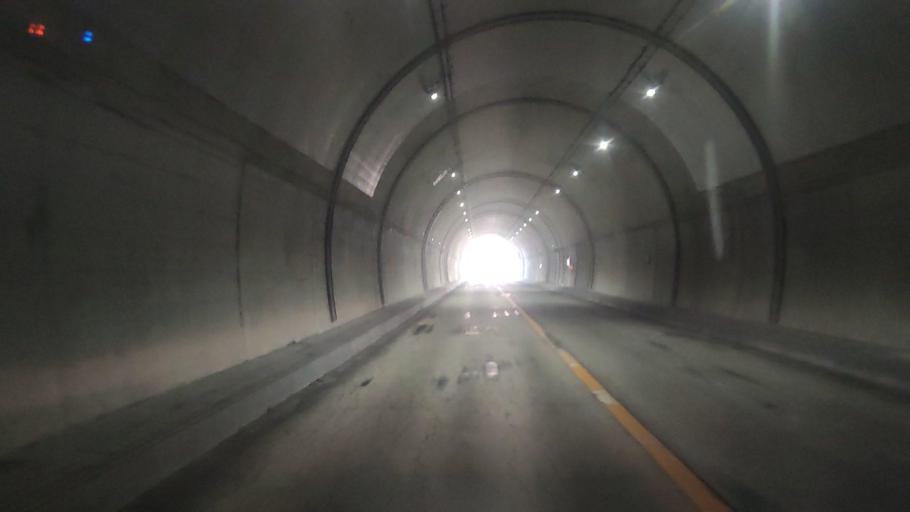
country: JP
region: Oita
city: Saiki
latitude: 32.8861
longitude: 131.9446
